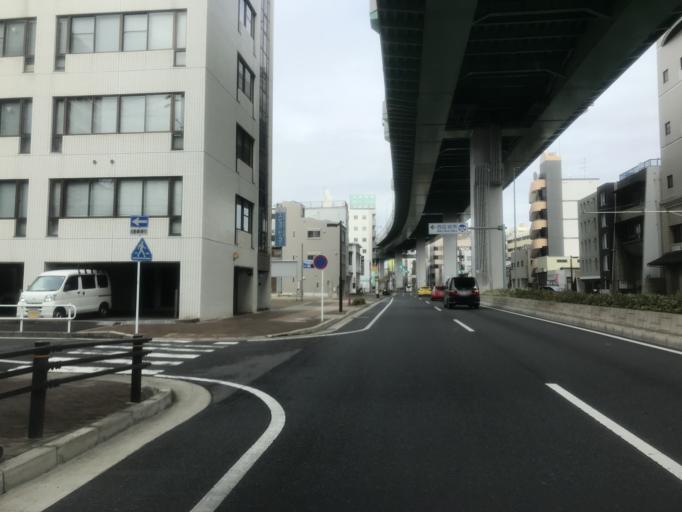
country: JP
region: Aichi
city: Nagoya-shi
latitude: 35.1880
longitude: 136.8908
